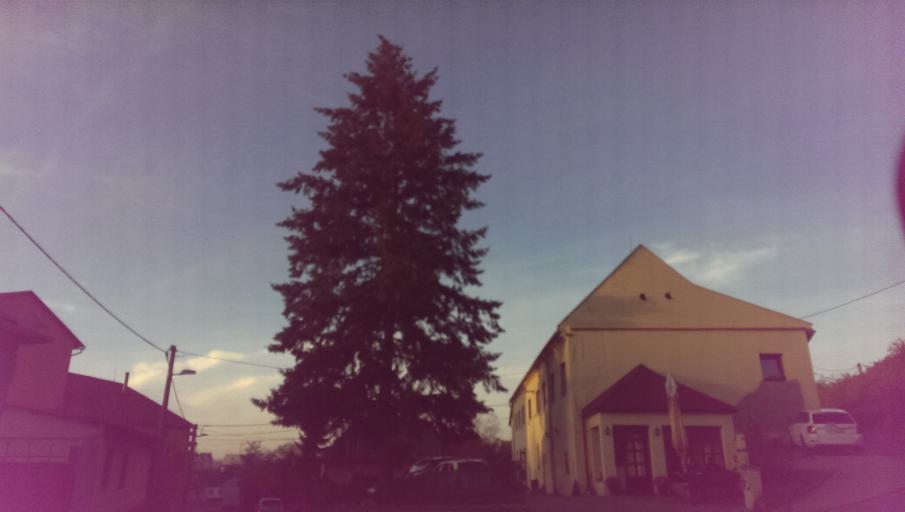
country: CZ
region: Zlin
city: Tecovice
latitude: 49.2048
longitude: 17.5982
